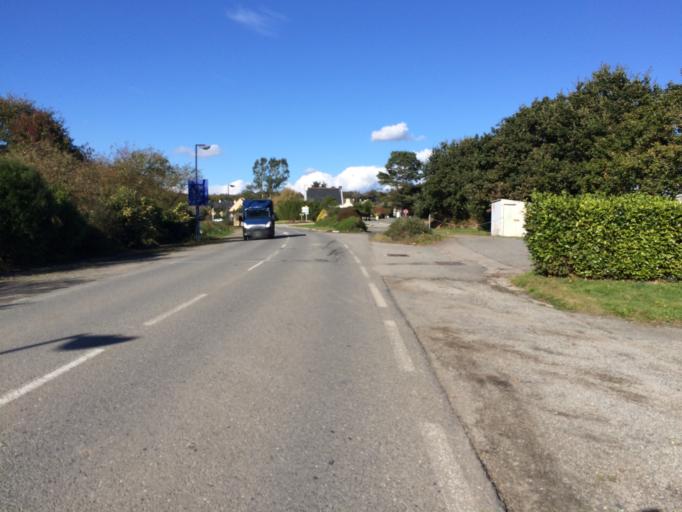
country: FR
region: Brittany
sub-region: Departement du Finistere
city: Saint-Urbain
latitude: 48.4032
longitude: -4.2282
